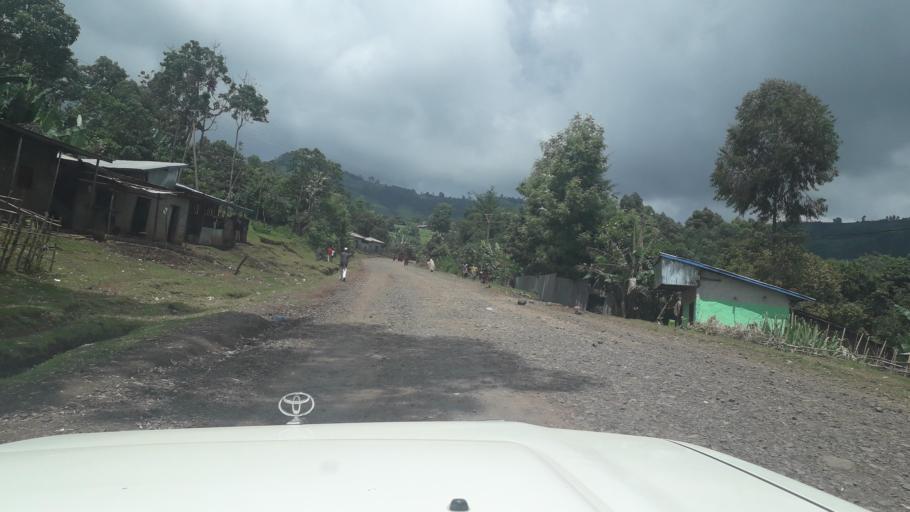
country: ET
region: Oromiya
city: Jima
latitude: 7.4239
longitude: 36.8729
